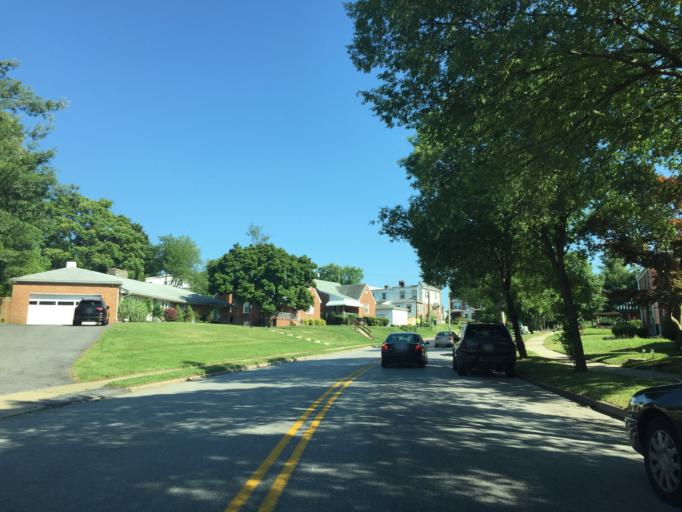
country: US
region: Maryland
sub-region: Baltimore County
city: Parkville
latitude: 39.3419
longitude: -76.5678
